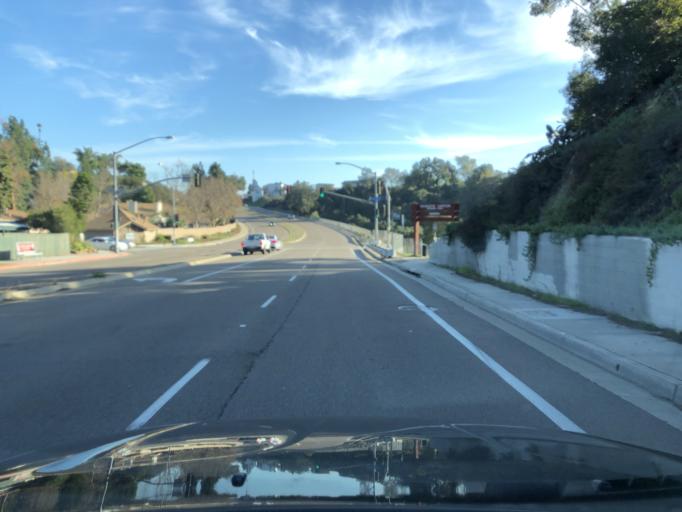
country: US
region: California
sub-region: San Diego County
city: La Jolla
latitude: 32.8292
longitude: -117.1937
